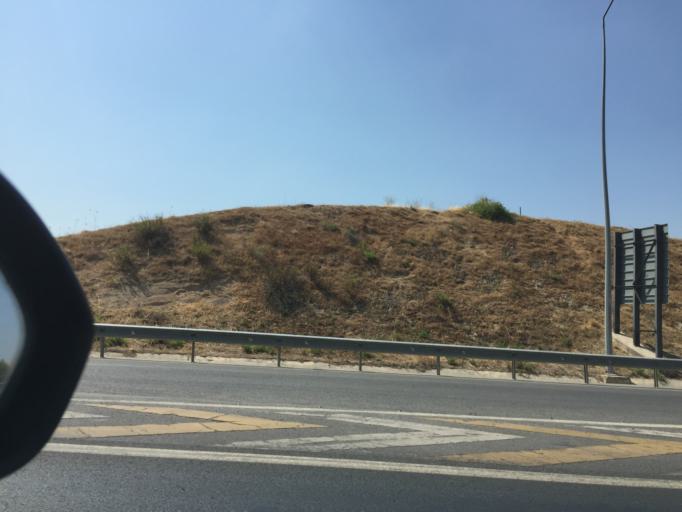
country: TR
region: Izmir
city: Karsiyaka
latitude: 38.4858
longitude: 27.1350
